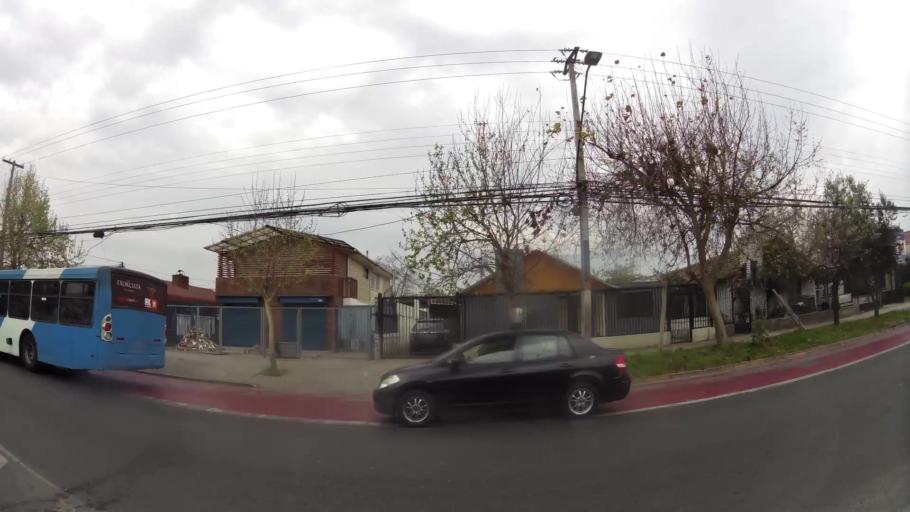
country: CL
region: Santiago Metropolitan
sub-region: Provincia de Santiago
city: Villa Presidente Frei, Nunoa, Santiago, Chile
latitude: -33.4916
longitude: -70.5997
